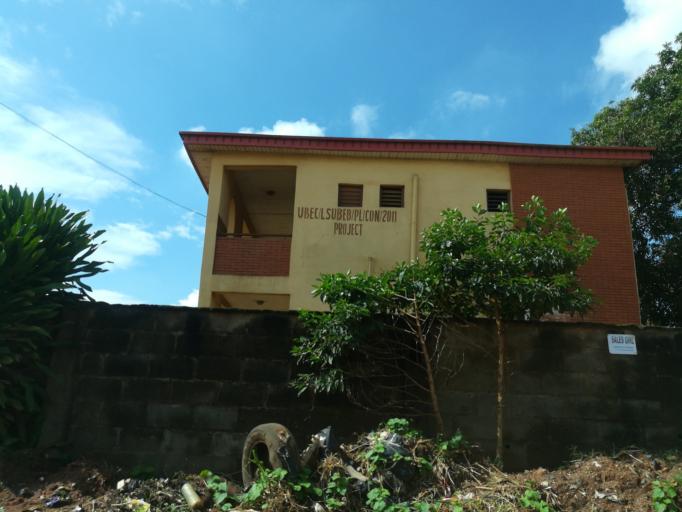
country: NG
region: Lagos
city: Ikorodu
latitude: 6.5928
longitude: 3.5213
